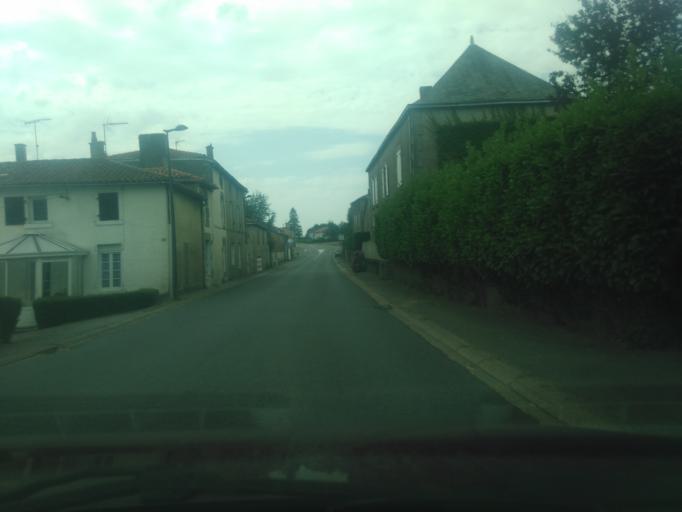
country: FR
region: Poitou-Charentes
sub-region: Departement des Deux-Sevres
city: Moncoutant
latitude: 46.6444
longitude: -0.5995
